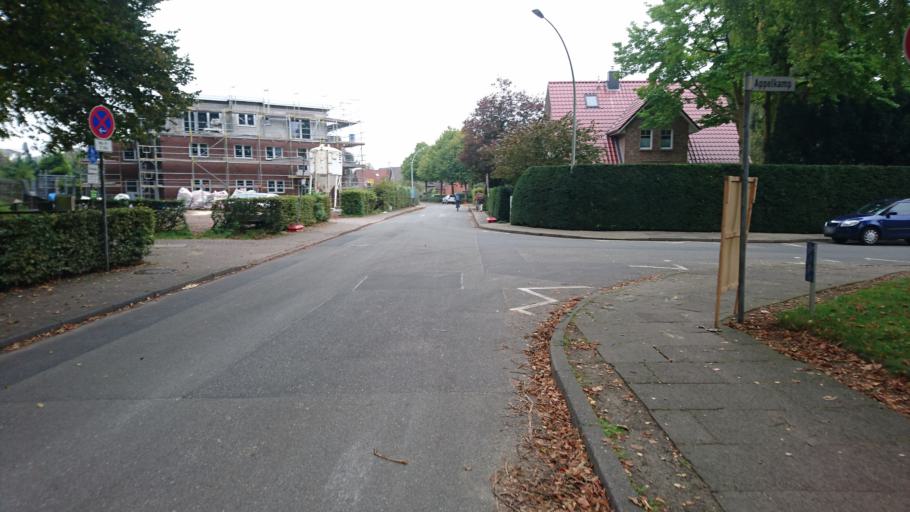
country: DE
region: Schleswig-Holstein
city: Rellingen
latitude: 53.6522
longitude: 9.8334
